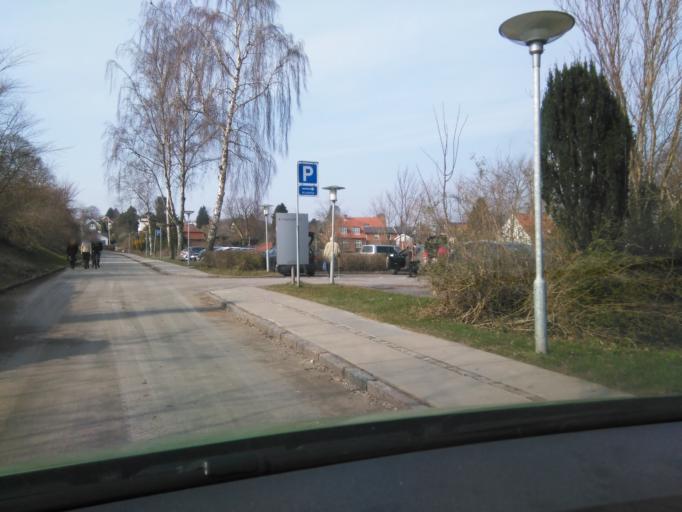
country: DK
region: Central Jutland
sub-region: Arhus Kommune
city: Arhus
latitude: 56.1870
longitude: 10.2329
